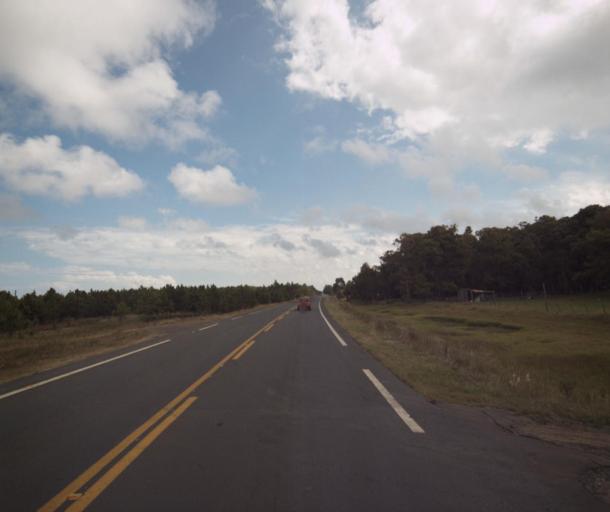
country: BR
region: Rio Grande do Sul
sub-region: Tapes
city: Tapes
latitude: -31.4115
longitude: -51.1695
